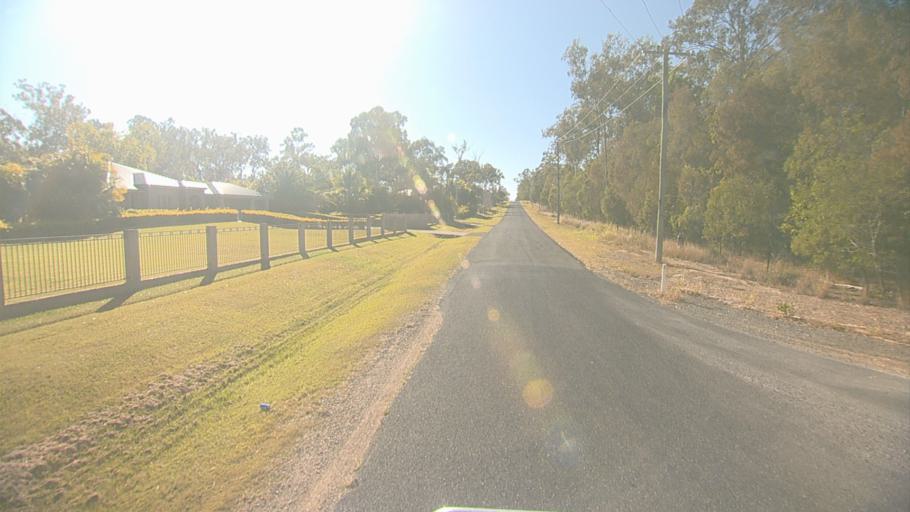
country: AU
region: Queensland
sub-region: Logan
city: Park Ridge South
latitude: -27.7461
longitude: 153.0374
